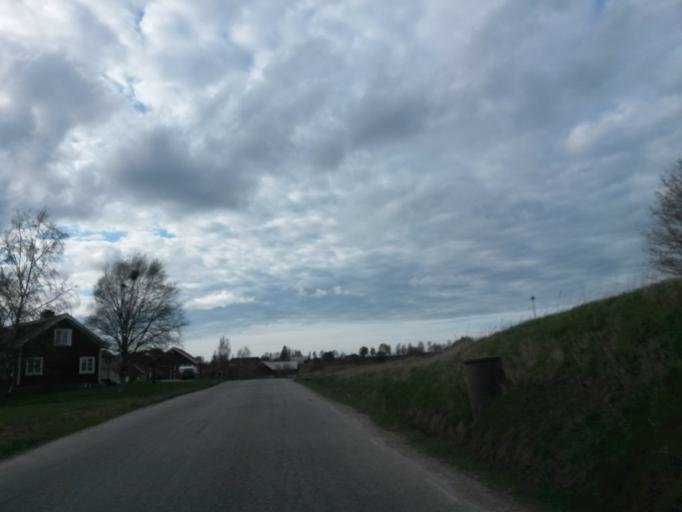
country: SE
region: Vaestra Goetaland
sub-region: Vargarda Kommun
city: Jonstorp
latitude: 57.9744
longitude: 12.6634
